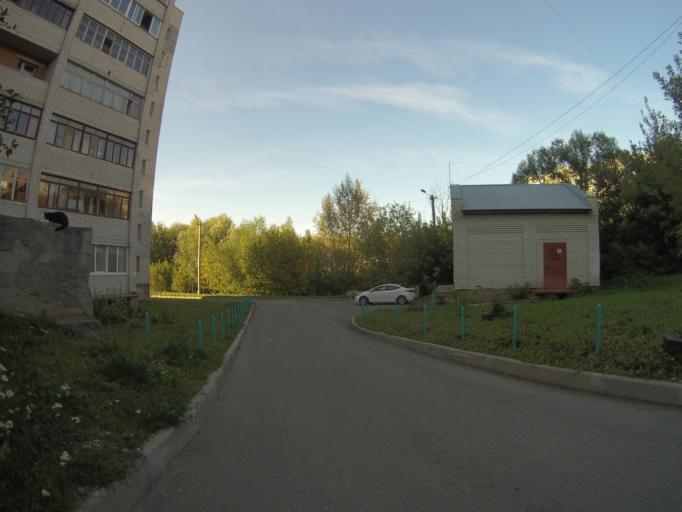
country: RU
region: Vladimir
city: Vladimir
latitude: 56.1490
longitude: 40.3640
